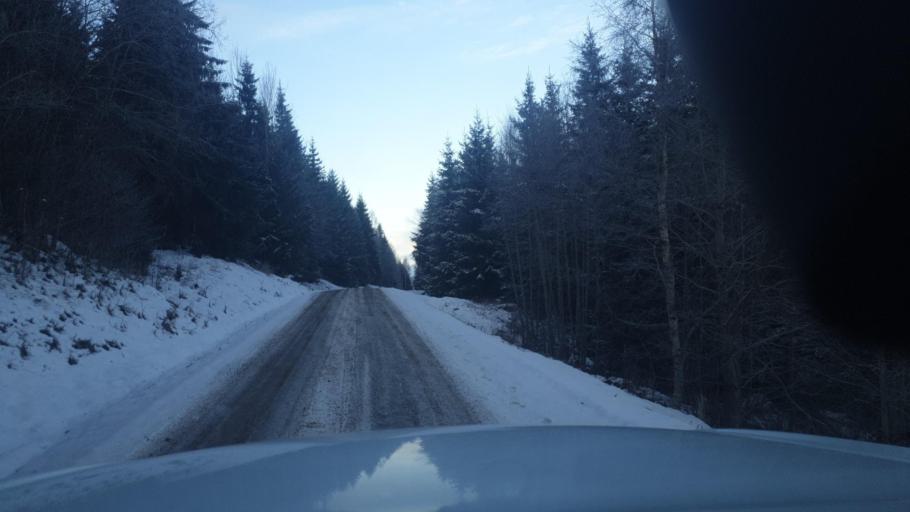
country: SE
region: Vaermland
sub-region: Arvika Kommun
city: Arvika
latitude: 60.0090
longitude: 12.6551
